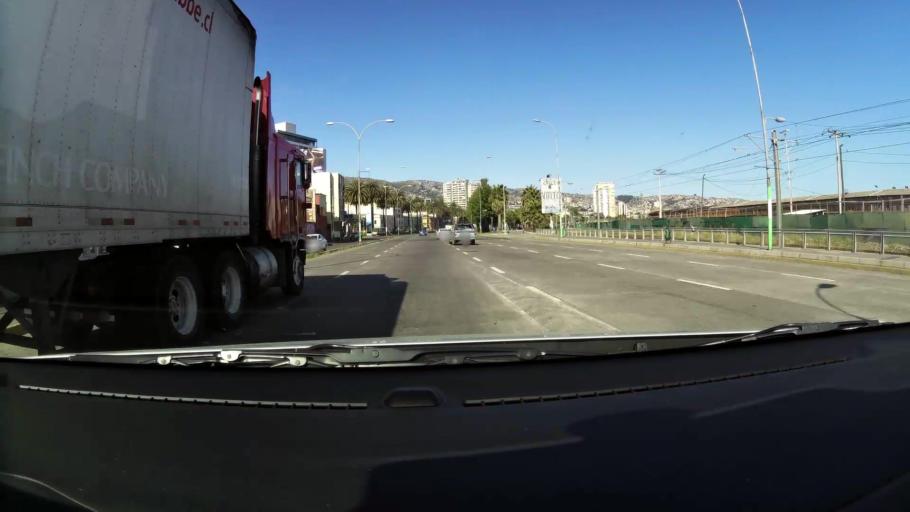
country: CL
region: Valparaiso
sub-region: Provincia de Valparaiso
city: Valparaiso
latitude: -33.0441
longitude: -71.6077
